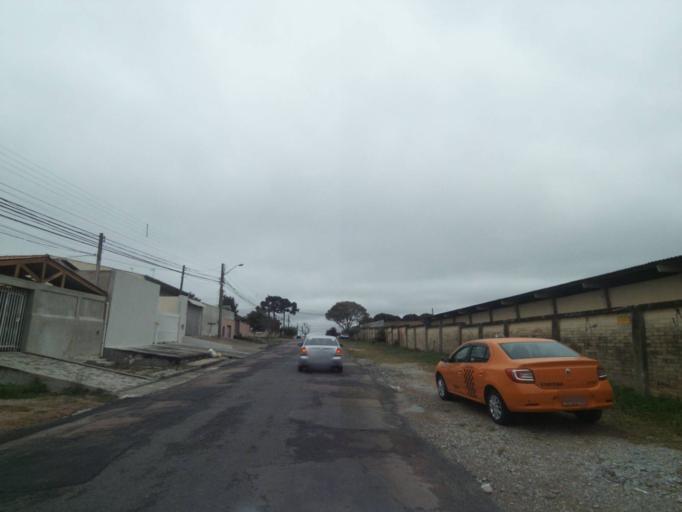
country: BR
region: Parana
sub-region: Curitiba
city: Curitiba
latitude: -25.5000
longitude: -49.3065
